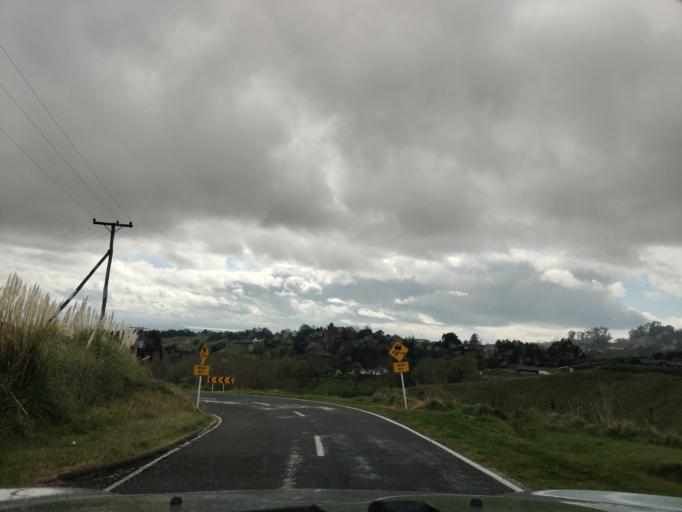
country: NZ
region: Hawke's Bay
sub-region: Hastings District
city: Hastings
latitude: -39.6901
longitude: 176.9006
